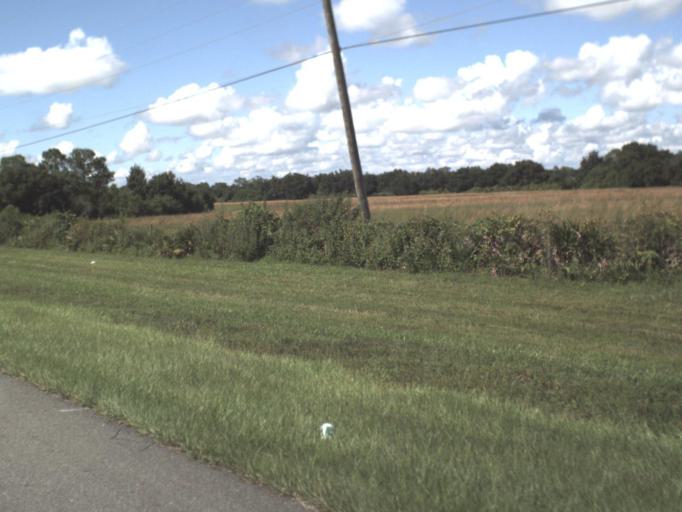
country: US
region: Florida
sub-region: Sarasota County
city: The Meadows
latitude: 27.4198
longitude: -82.3649
